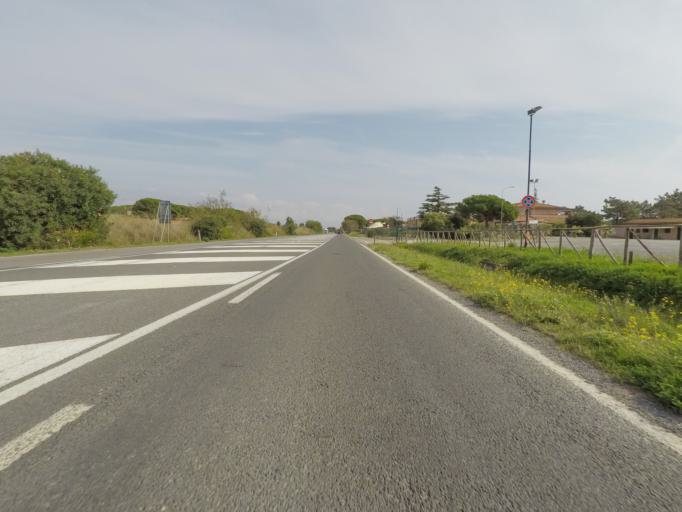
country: IT
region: Tuscany
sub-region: Provincia di Grosseto
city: Orbetello Scalo
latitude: 42.4152
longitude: 11.3225
